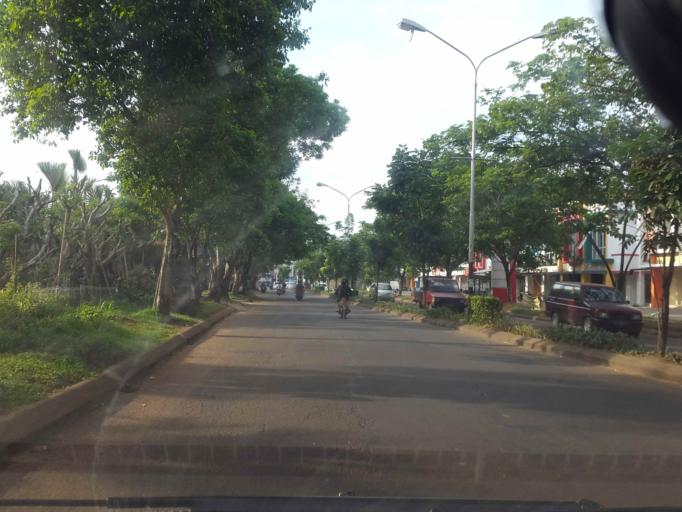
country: ID
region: West Java
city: Ciputat
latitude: -6.2632
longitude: 106.6875
